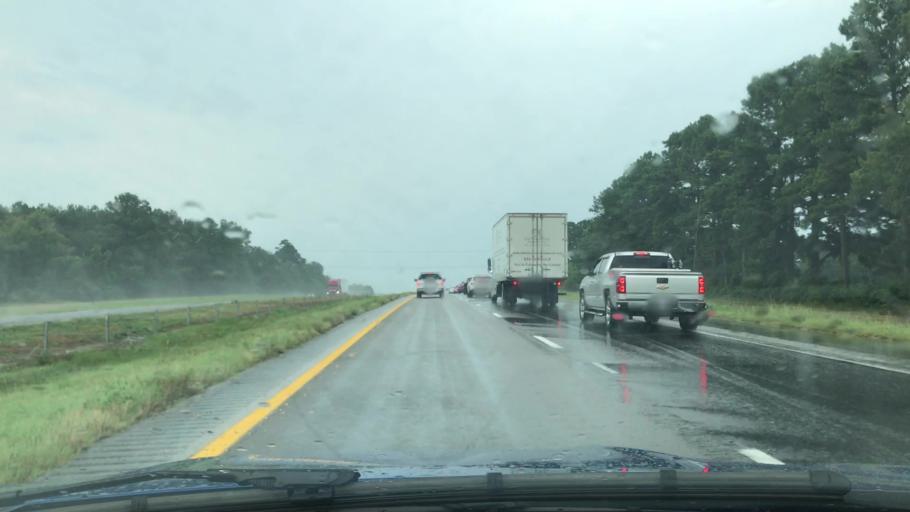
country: US
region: Texas
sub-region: Harrison County
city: Waskom
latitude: 32.4906
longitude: -94.1479
